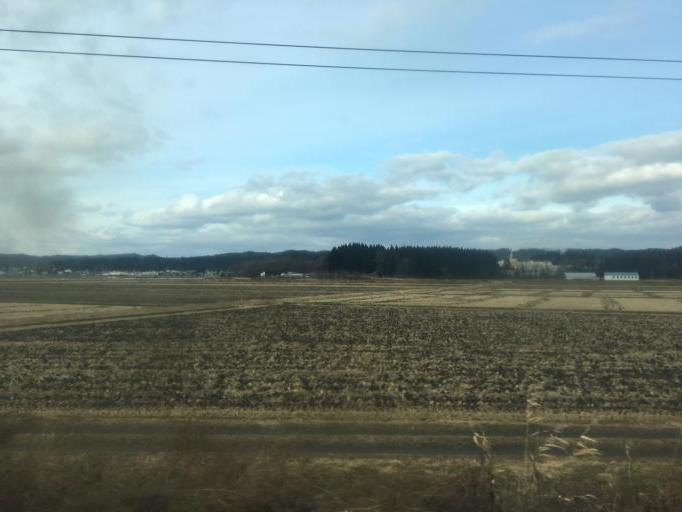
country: JP
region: Akita
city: Takanosu
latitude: 40.2481
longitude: 140.3945
